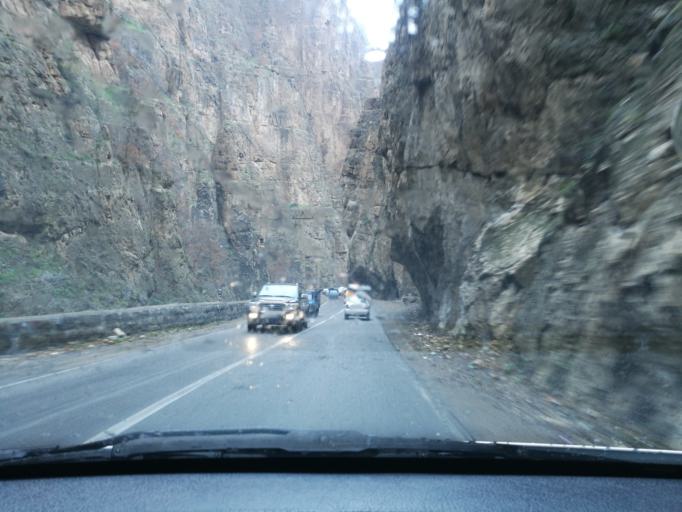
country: IR
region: Mazandaran
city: Chalus
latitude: 36.2718
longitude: 51.2447
